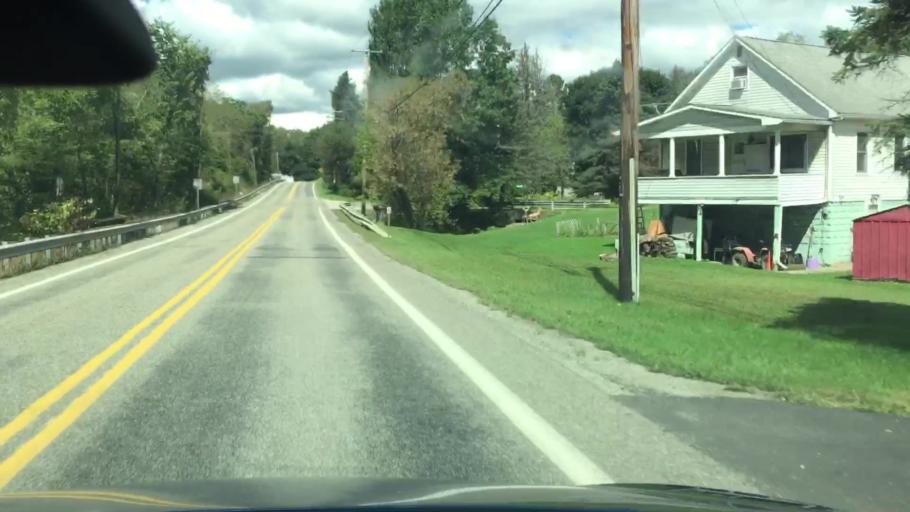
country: US
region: Pennsylvania
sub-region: Allegheny County
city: Russellton
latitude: 40.6257
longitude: -79.8326
